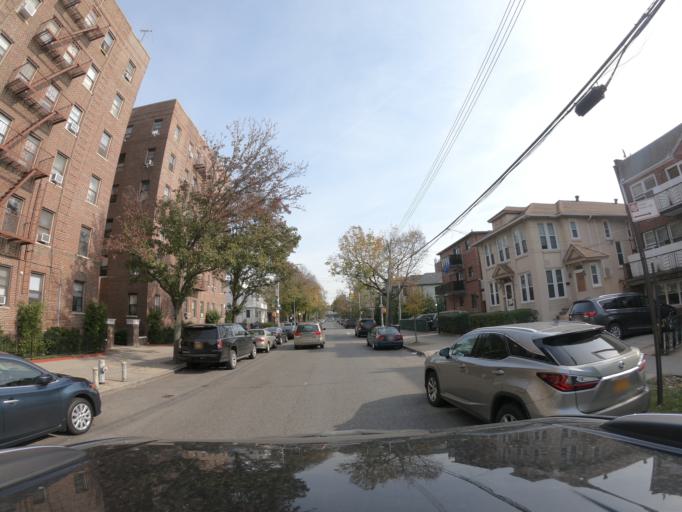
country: US
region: New York
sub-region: Kings County
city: Bensonhurst
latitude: 40.6154
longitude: -73.9619
